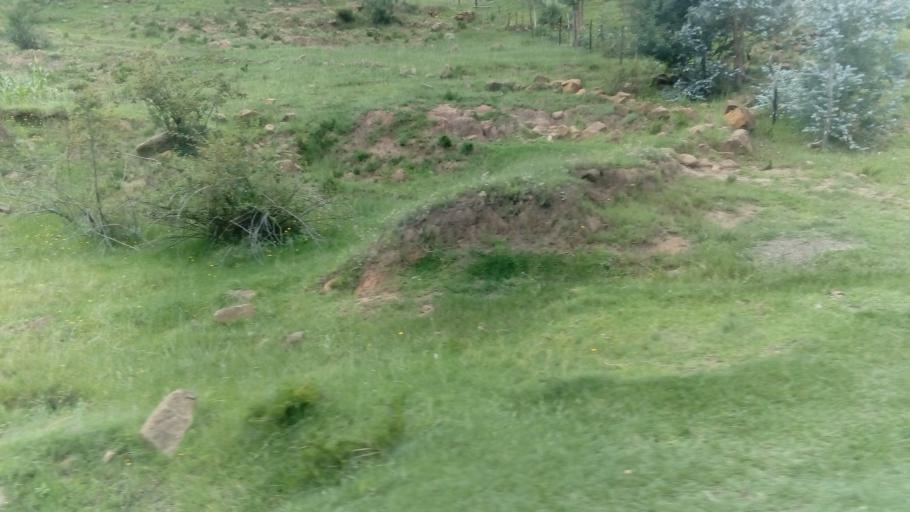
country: LS
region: Leribe
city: Leribe
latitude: -28.9659
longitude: 28.1728
